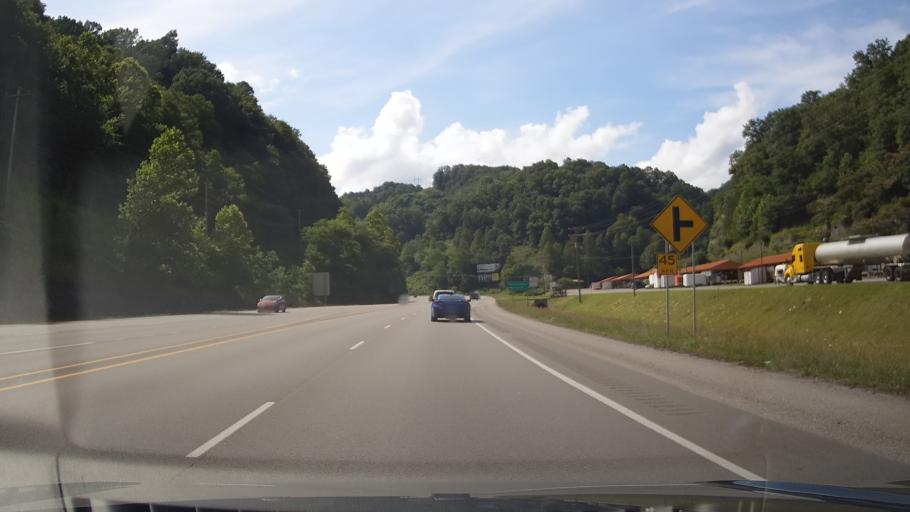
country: US
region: Kentucky
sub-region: Floyd County
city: Prestonsburg
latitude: 37.6396
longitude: -82.7549
